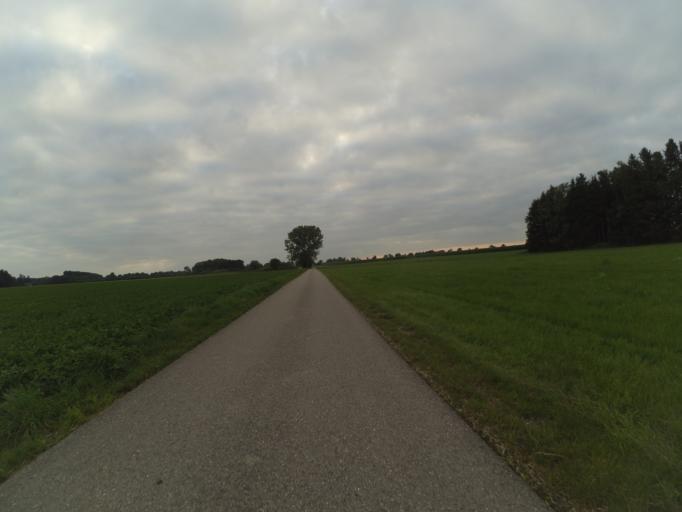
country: DE
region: Bavaria
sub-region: Swabia
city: Buchloe
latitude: 48.0457
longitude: 10.7637
